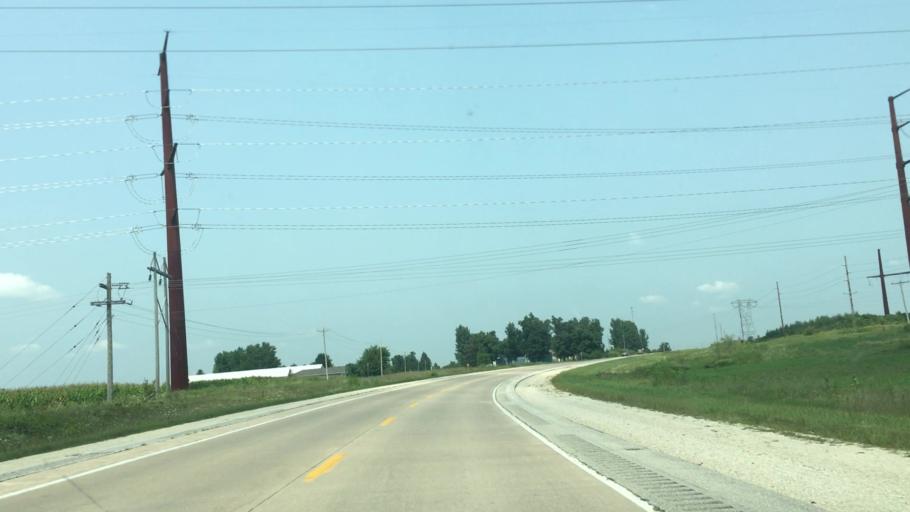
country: US
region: Iowa
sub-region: Fayette County
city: Oelwein
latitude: 42.5851
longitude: -91.9048
